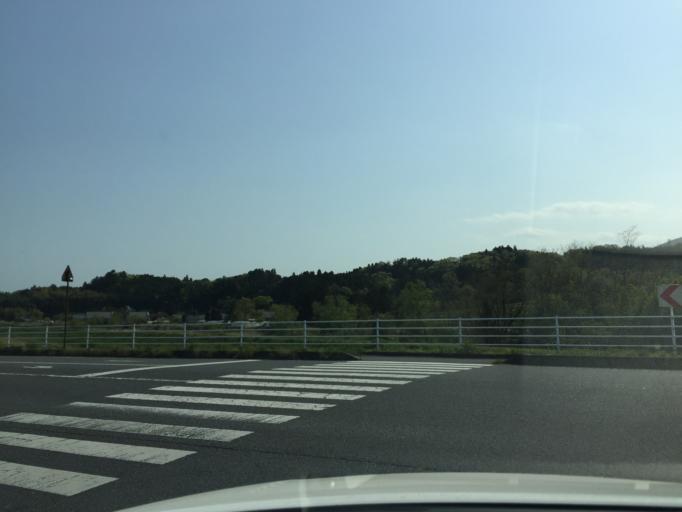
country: JP
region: Fukushima
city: Iwaki
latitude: 37.1343
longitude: 140.8522
